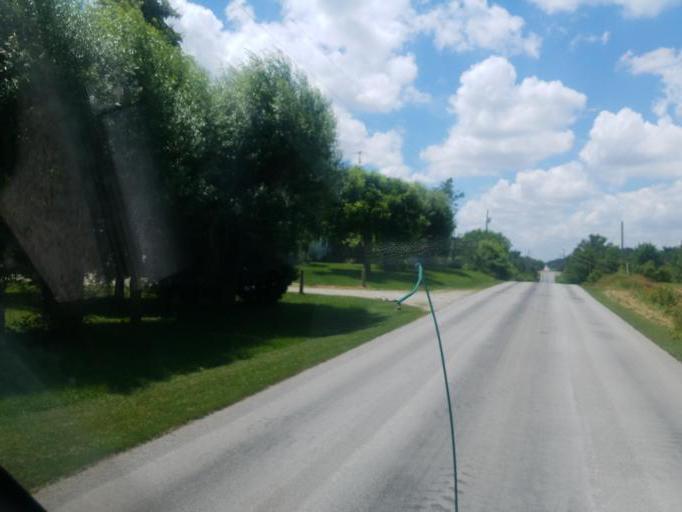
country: US
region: Ohio
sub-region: Huron County
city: Willard
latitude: 41.0792
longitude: -82.7141
